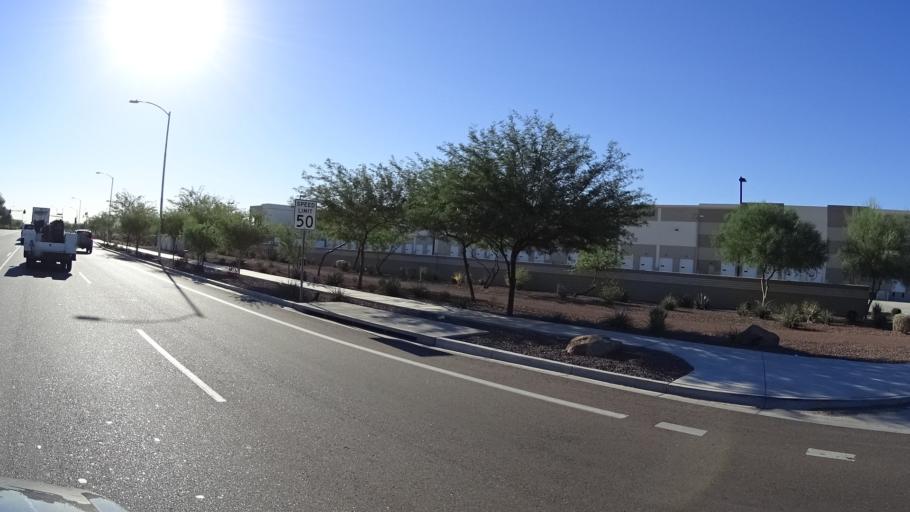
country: US
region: Arizona
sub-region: Maricopa County
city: Laveen
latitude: 33.4224
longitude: -112.1803
